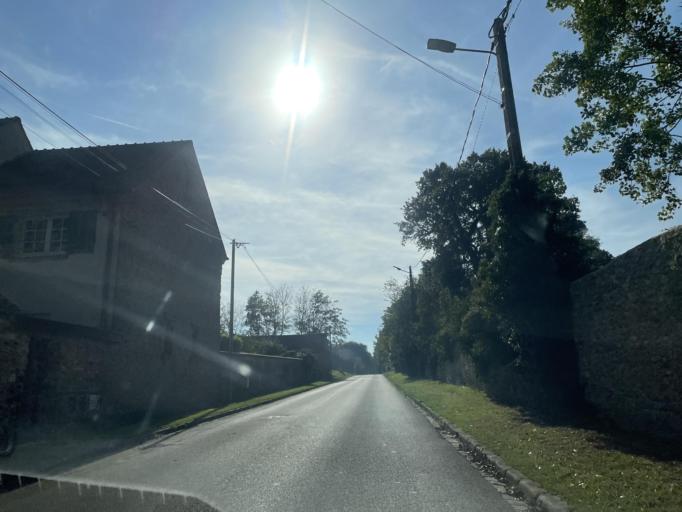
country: FR
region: Ile-de-France
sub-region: Departement de Seine-et-Marne
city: Saint-Jean-les-Deux-Jumeaux
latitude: 48.9401
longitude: 2.9856
